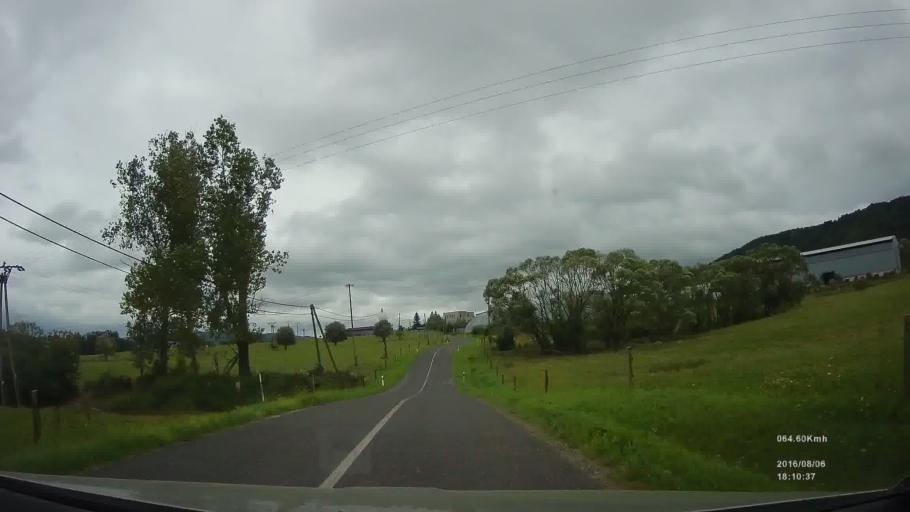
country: SK
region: Presovsky
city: Svidnik
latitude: 49.3692
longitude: 21.5754
